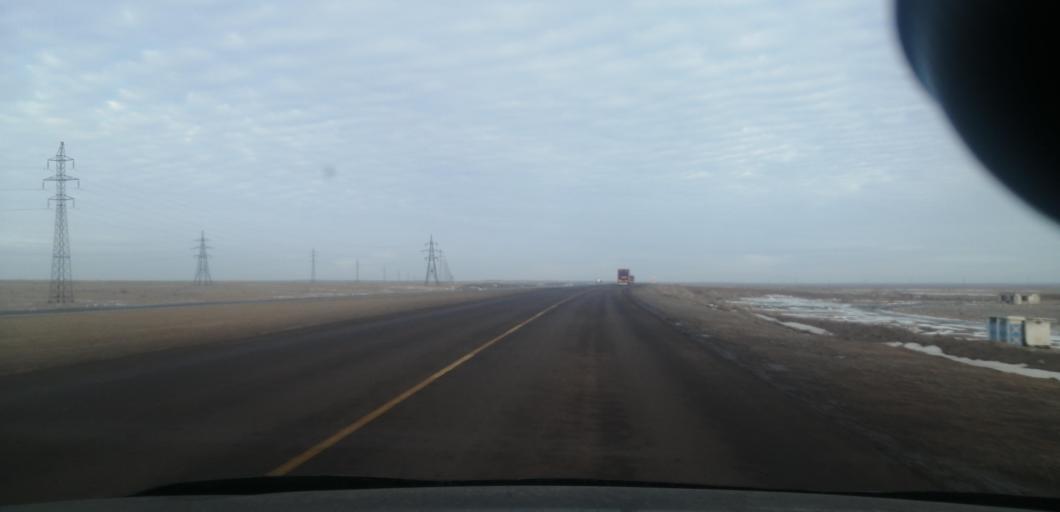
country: KZ
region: Qaraghandy
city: Balqash
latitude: 46.8049
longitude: 74.7013
